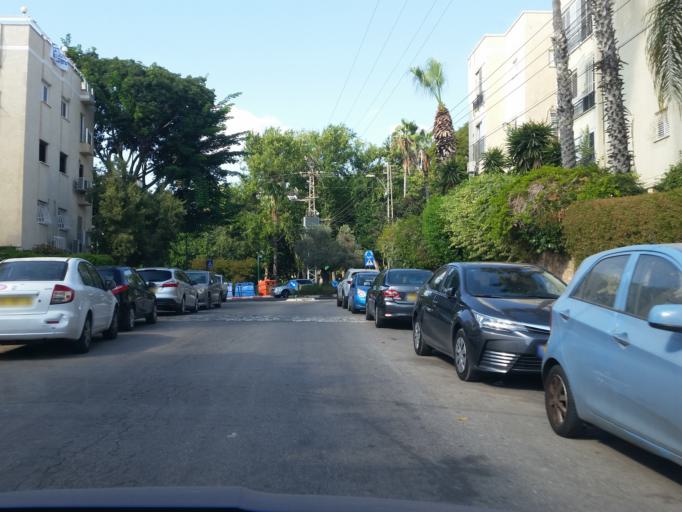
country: IL
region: Tel Aviv
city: Ramat HaSharon
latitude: 32.1414
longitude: 34.8406
